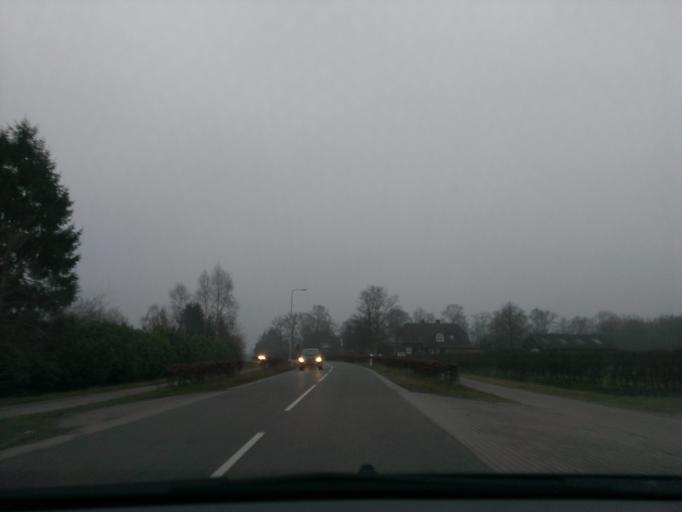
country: NL
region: Gelderland
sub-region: Gemeente Voorst
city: Twello
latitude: 52.2518
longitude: 6.1126
